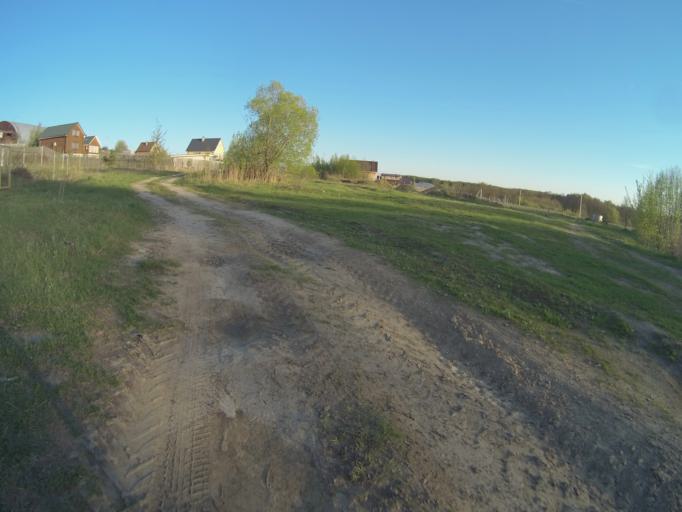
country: RU
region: Vladimir
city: Kommunar
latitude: 56.0839
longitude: 40.4909
